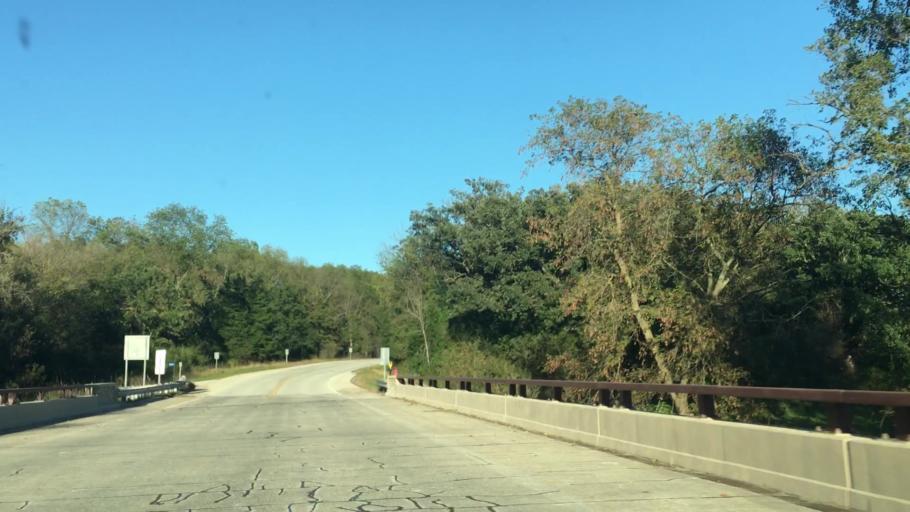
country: US
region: Minnesota
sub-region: Fillmore County
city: Chatfield
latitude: 43.8178
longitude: -92.0500
